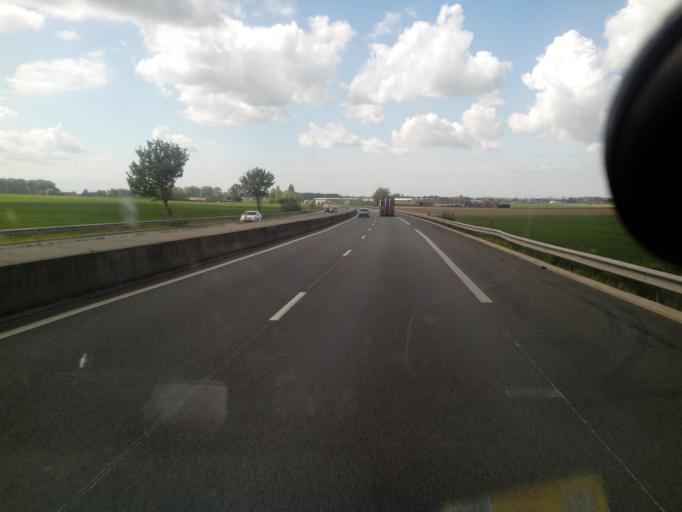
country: FR
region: Nord-Pas-de-Calais
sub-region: Departement du Nord
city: Quaedypre
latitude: 50.9401
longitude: 2.4585
